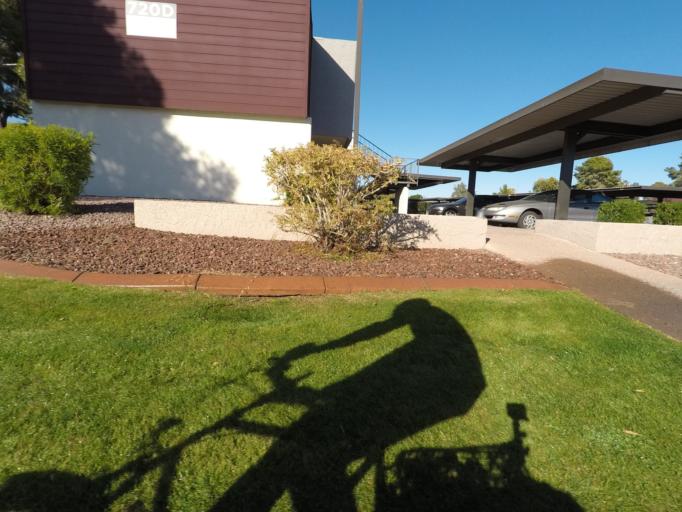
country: US
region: Arizona
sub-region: Maricopa County
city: Tempe Junction
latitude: 33.4513
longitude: -111.9281
